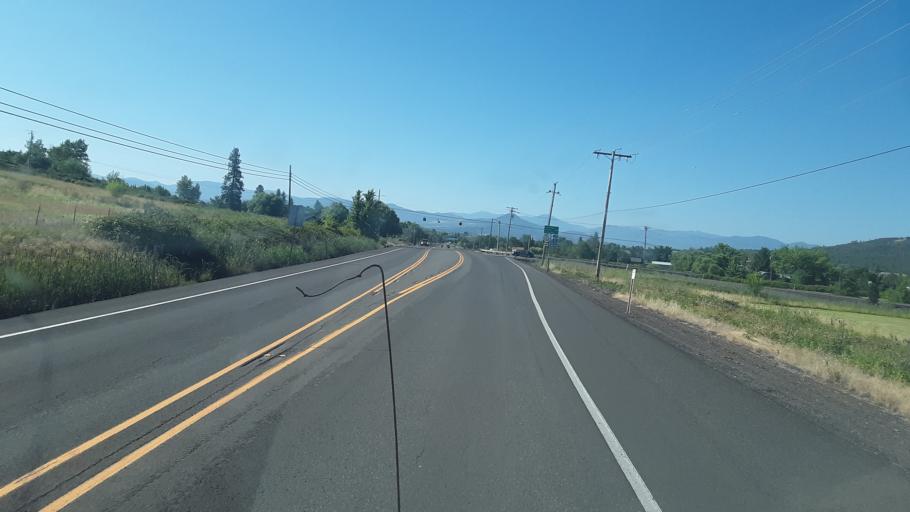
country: US
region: Oregon
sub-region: Jackson County
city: Eagle Point
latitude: 42.5251
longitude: -122.8144
